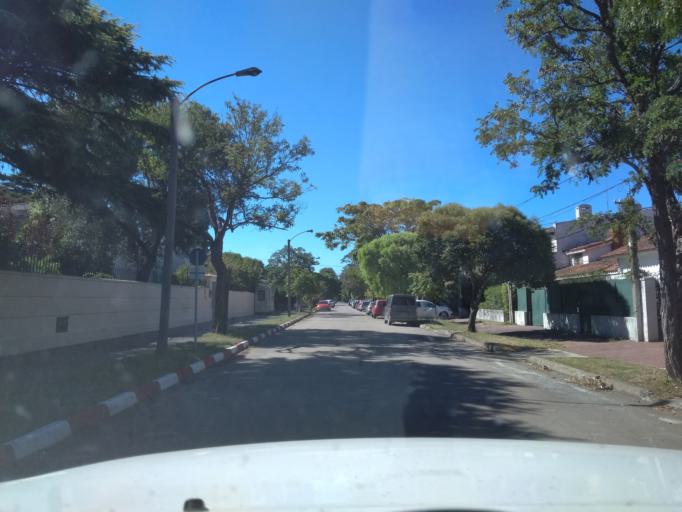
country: UY
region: Canelones
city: Paso de Carrasco
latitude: -34.8921
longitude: -56.0614
